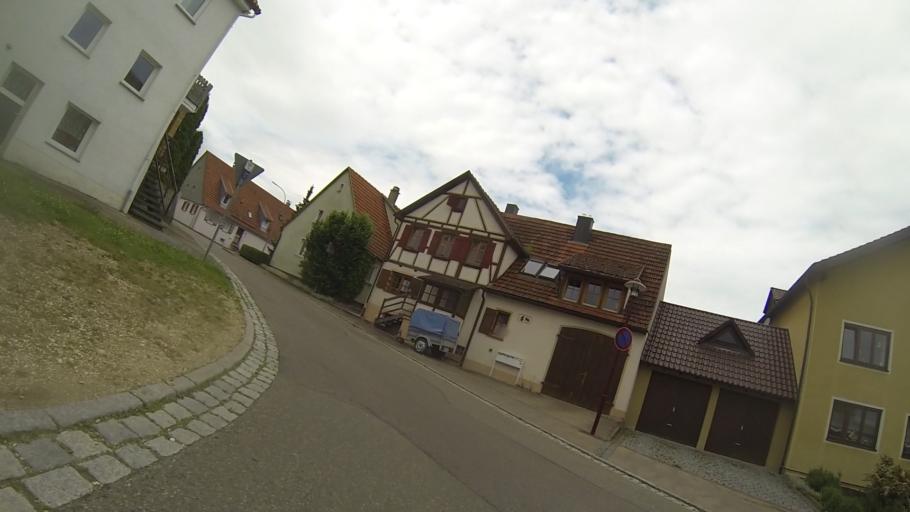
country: DE
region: Baden-Wuerttemberg
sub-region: Regierungsbezirk Stuttgart
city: Steinheim am Albuch
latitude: 48.6900
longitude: 10.0674
